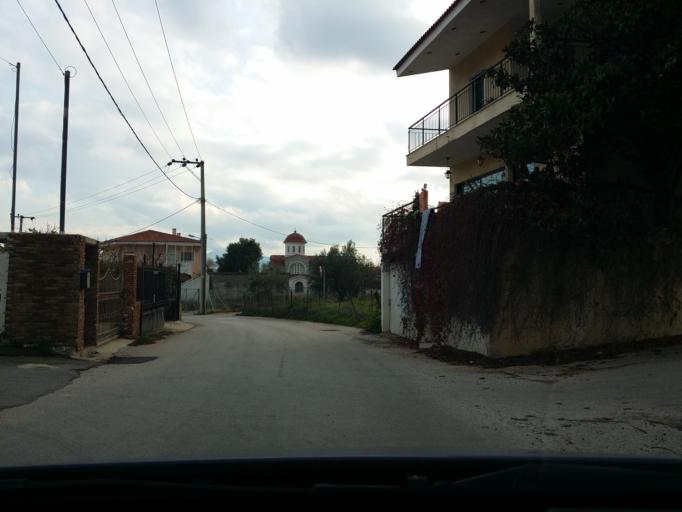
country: GR
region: Attica
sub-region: Nomarchia Anatolikis Attikis
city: Polydendri
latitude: 38.2163
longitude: 23.8660
